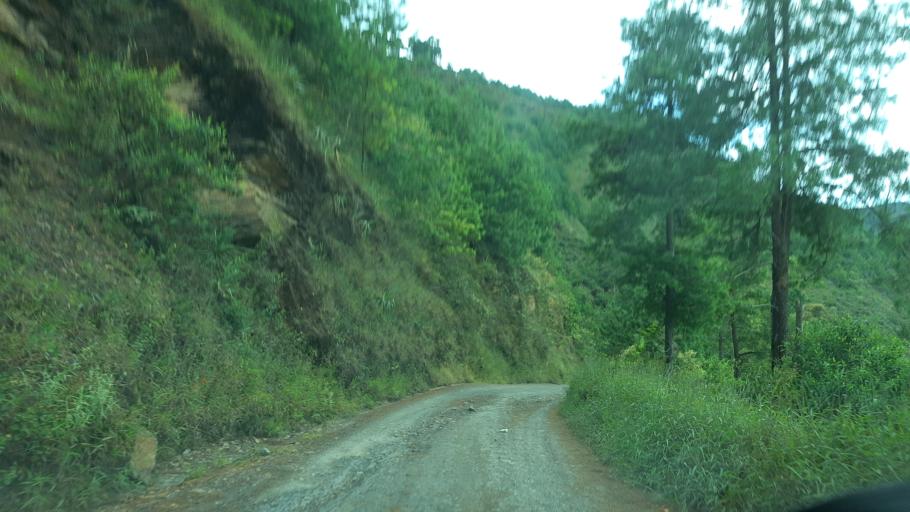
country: CO
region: Boyaca
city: Garagoa
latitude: 5.0003
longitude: -73.3350
